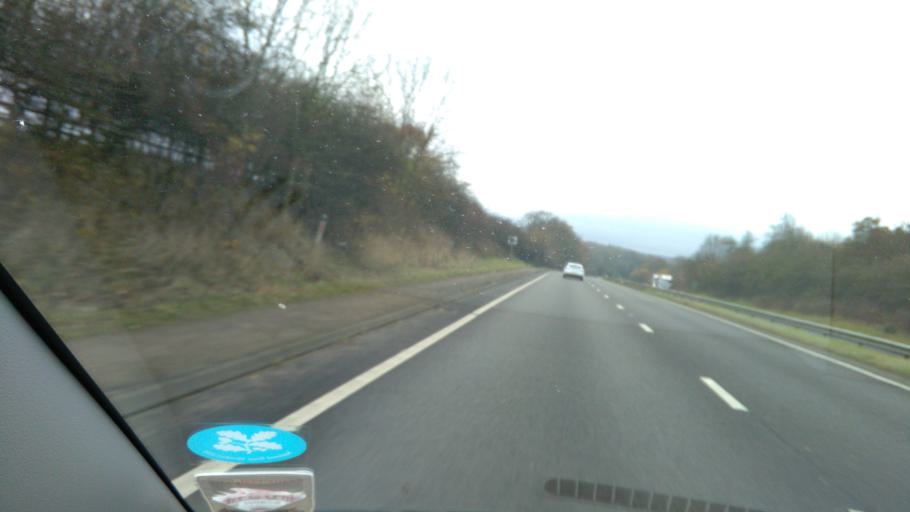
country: GB
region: England
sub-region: Northamptonshire
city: Blisworth
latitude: 52.1575
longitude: -0.9651
